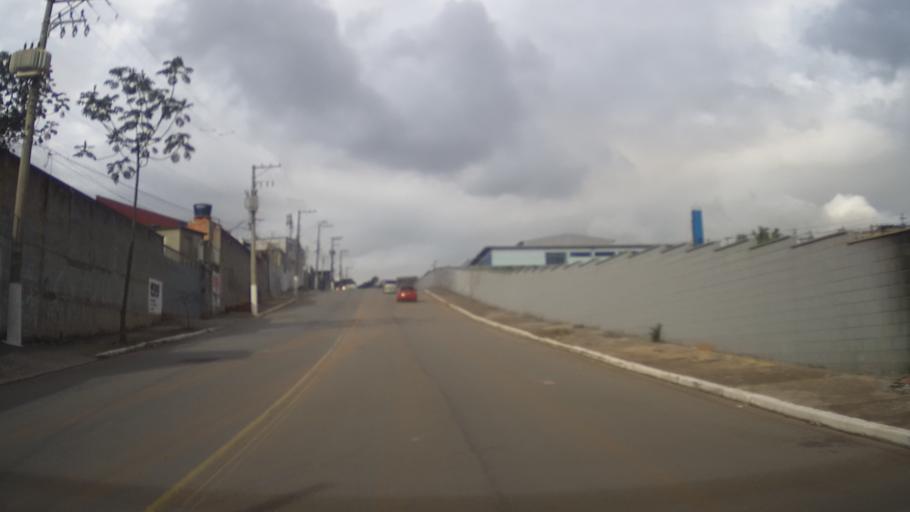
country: BR
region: Sao Paulo
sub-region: Itaquaquecetuba
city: Itaquaquecetuba
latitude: -23.4540
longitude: -46.4258
